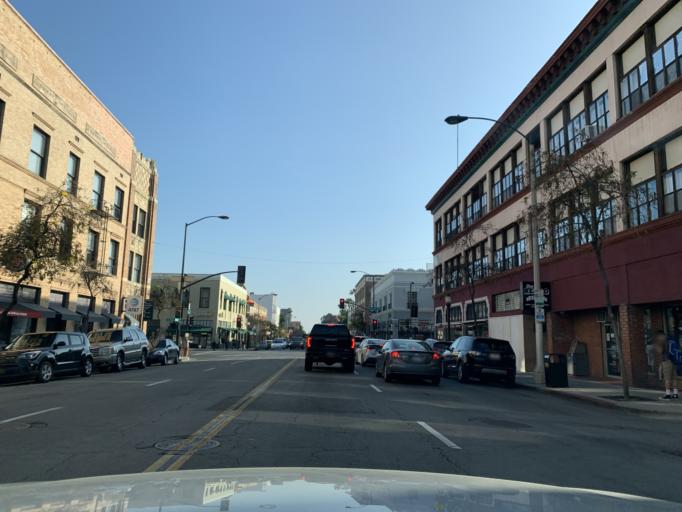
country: US
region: California
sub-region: Los Angeles County
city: Pasadena
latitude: 34.1463
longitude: -118.1489
